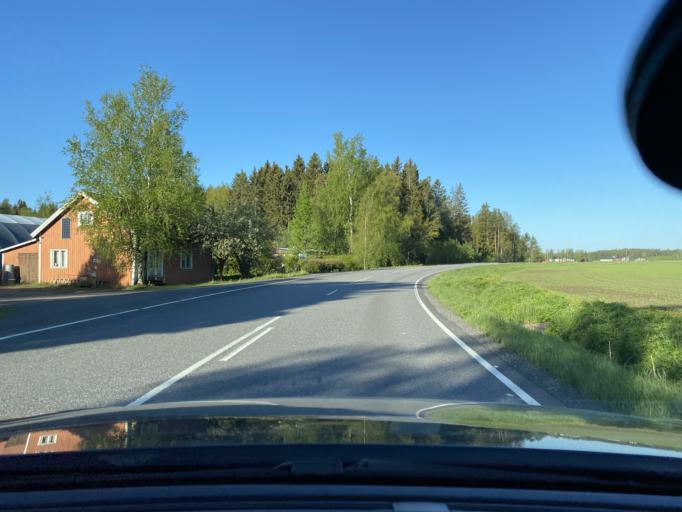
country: FI
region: Varsinais-Suomi
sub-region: Loimaa
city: Alastaro
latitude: 60.8779
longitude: 22.8125
